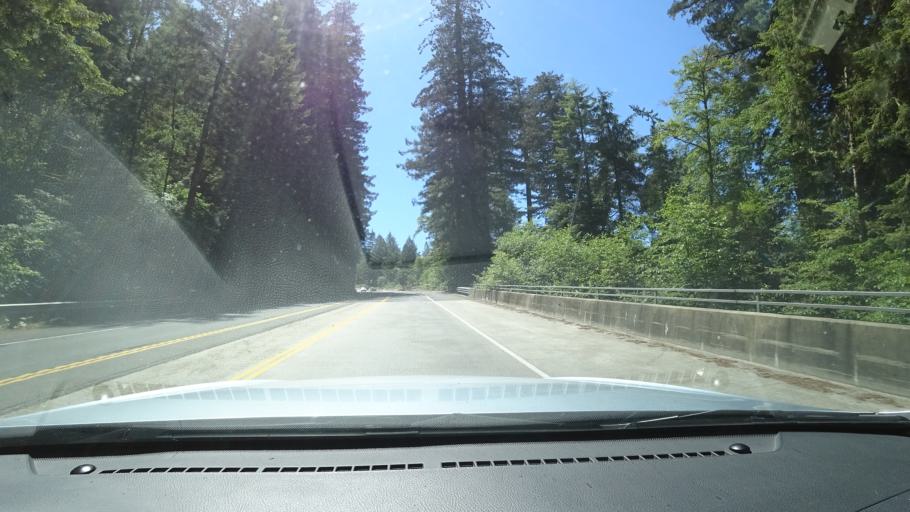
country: US
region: California
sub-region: Del Norte County
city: Bertsch-Oceanview
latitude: 41.7103
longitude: -124.1265
